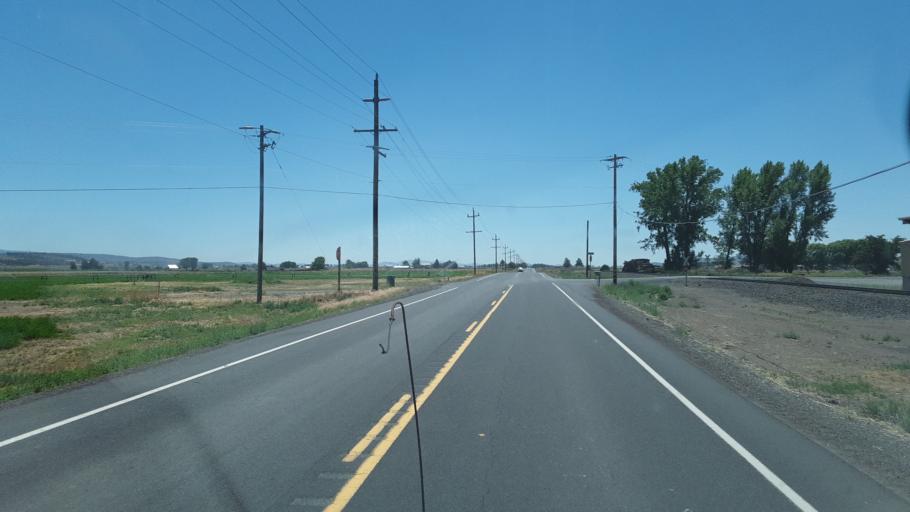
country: US
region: Oregon
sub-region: Klamath County
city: Altamont
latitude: 42.0661
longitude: -121.6598
